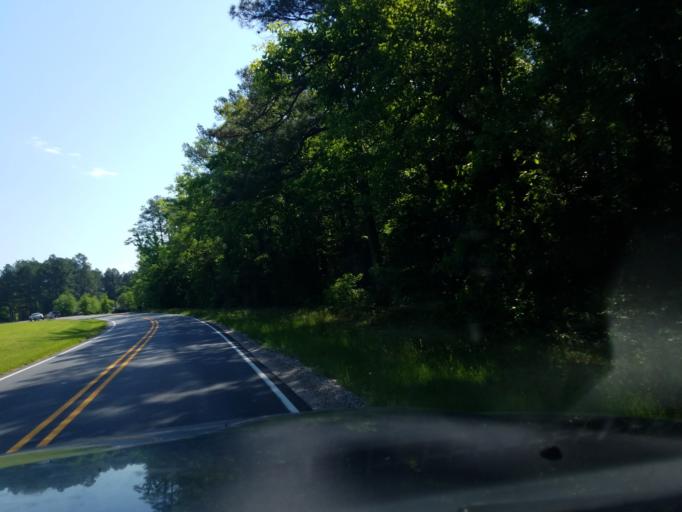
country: US
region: North Carolina
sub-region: Vance County
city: Henderson
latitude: 36.3697
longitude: -78.4503
